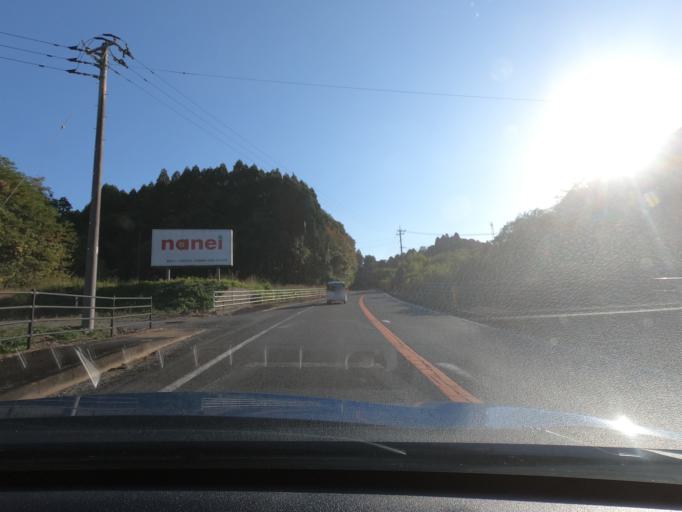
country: JP
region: Kagoshima
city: Akune
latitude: 32.0527
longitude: 130.2212
